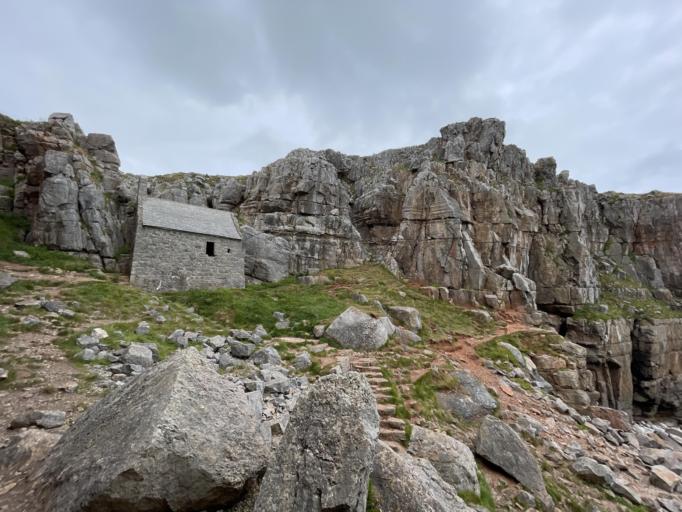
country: GB
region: Wales
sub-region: Pembrokeshire
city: Hundleton
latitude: 51.5985
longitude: -4.9367
